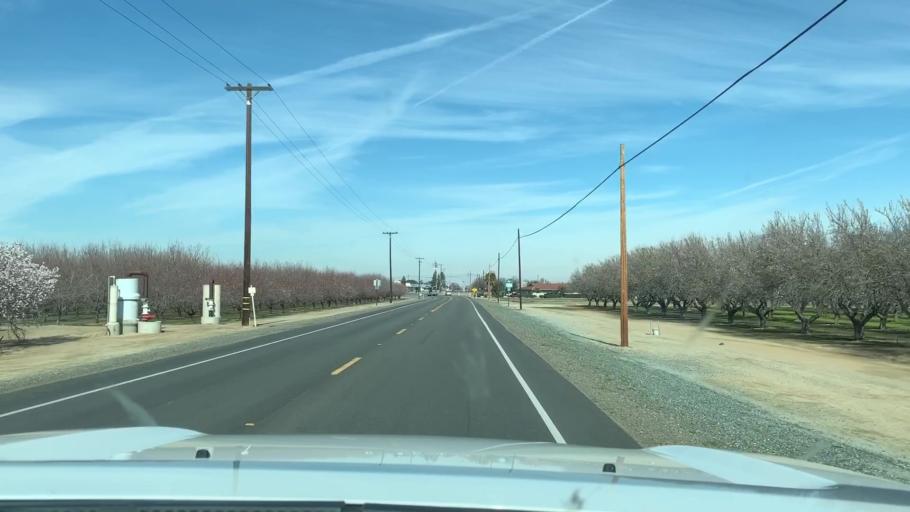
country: US
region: California
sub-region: Kern County
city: Shafter
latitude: 35.4886
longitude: -119.2607
